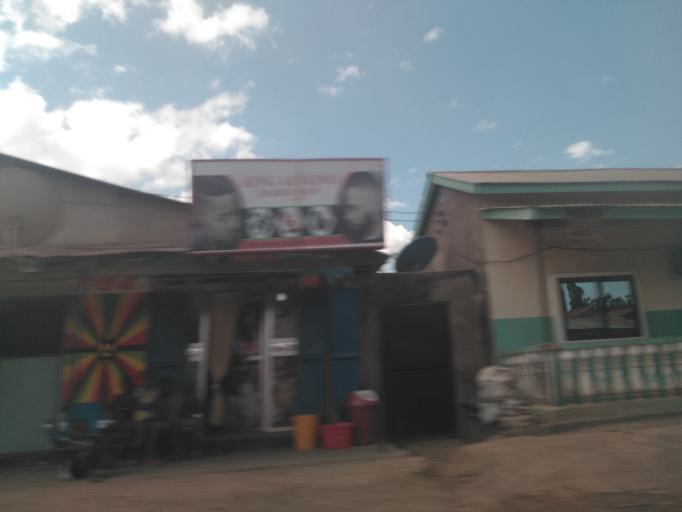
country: TZ
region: Dar es Salaam
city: Dar es Salaam
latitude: -6.8718
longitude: 39.2369
